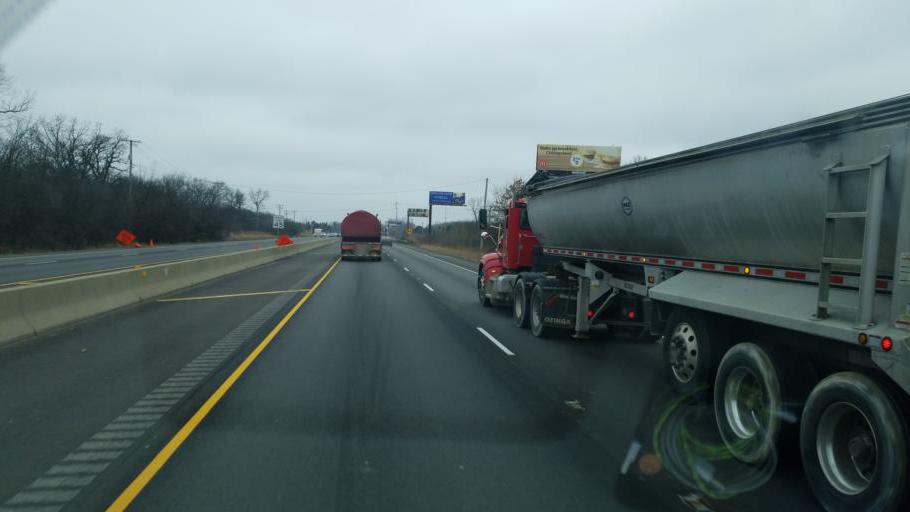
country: US
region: Illinois
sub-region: Lake County
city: Knollwood
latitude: 42.3162
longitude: -87.8792
